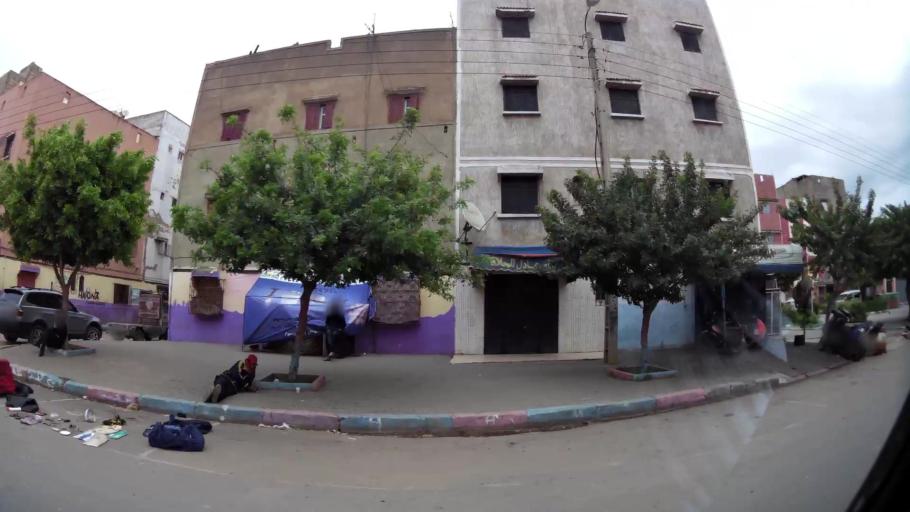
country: MA
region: Grand Casablanca
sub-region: Mediouna
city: Tit Mellil
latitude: 33.5621
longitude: -7.5439
